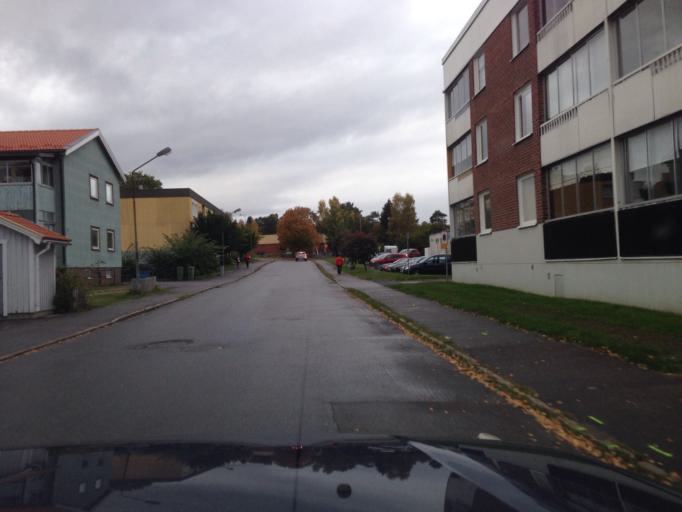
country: SE
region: Vaesternorrland
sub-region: Sundsvalls Kommun
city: Sundsvall
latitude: 62.3997
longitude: 17.3305
